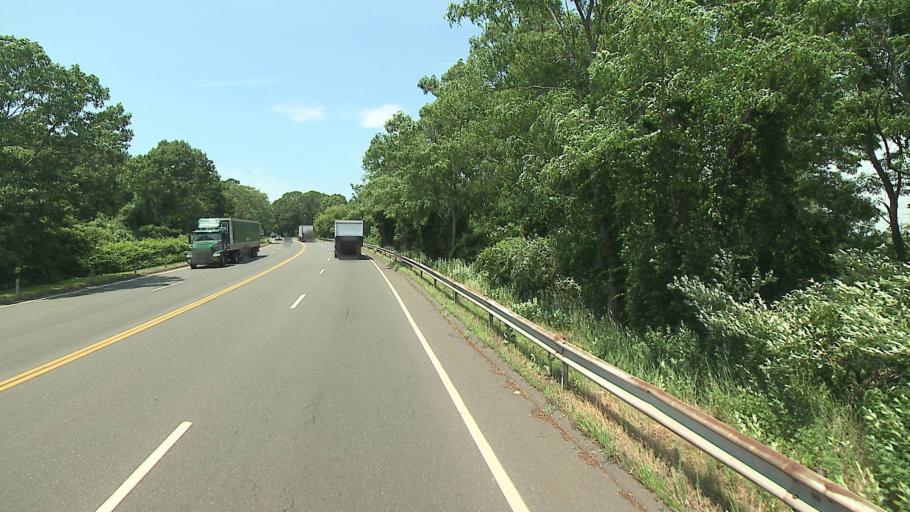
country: US
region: Connecticut
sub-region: New Haven County
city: Hamden
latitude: 41.3807
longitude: -72.8859
